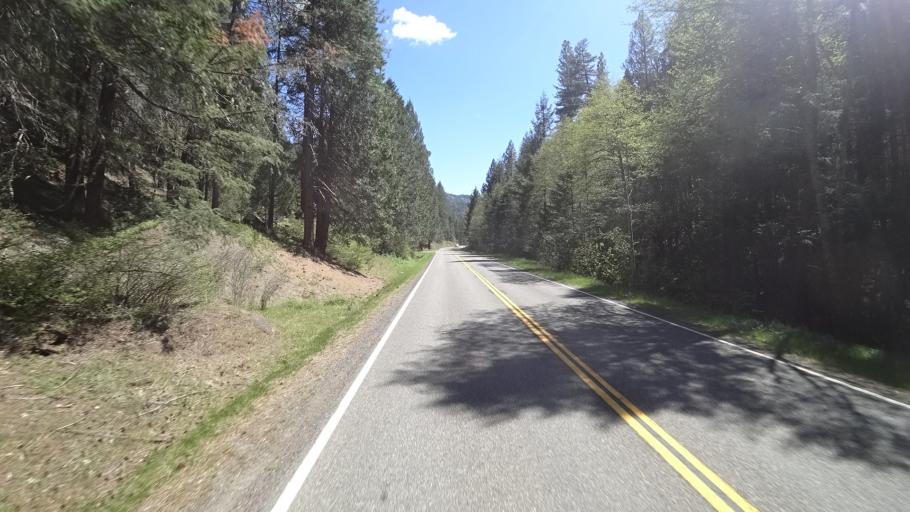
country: US
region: California
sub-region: Trinity County
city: Weaverville
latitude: 40.7644
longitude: -122.8884
